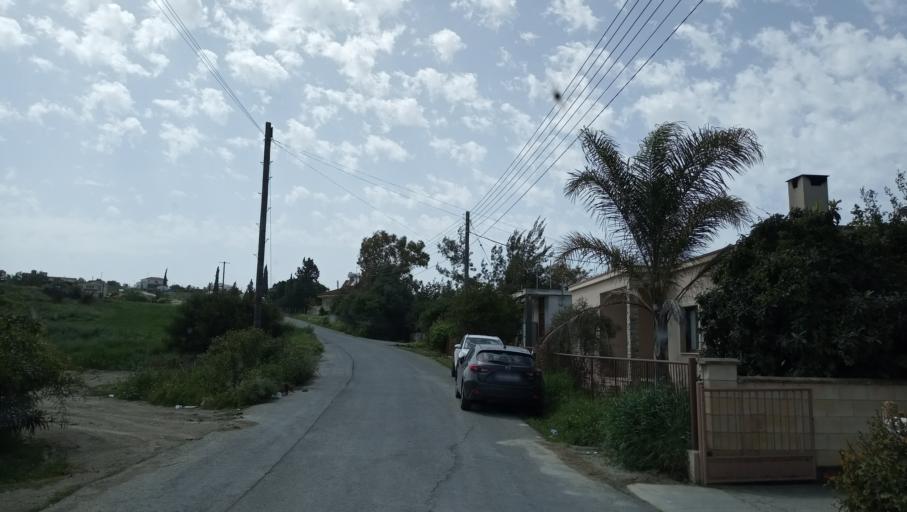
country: CY
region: Lefkosia
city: Dali
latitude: 35.0187
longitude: 33.4210
